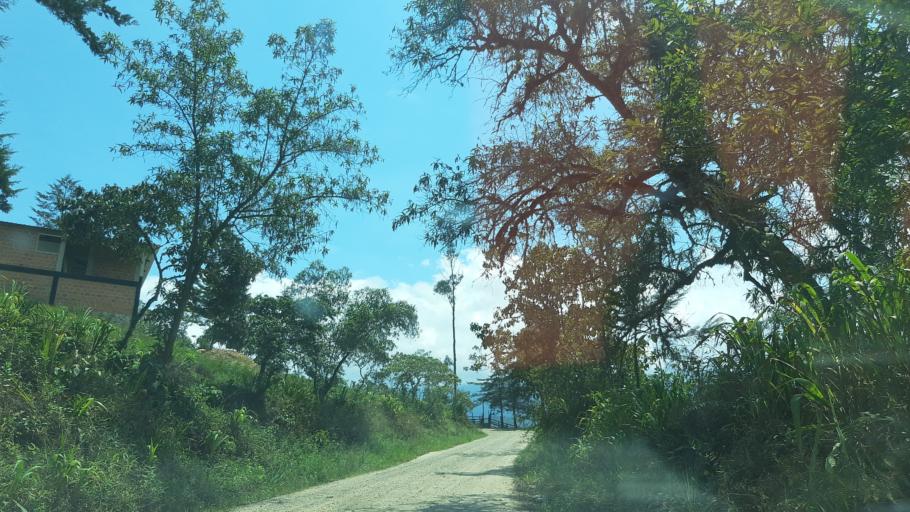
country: CO
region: Boyaca
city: Chinavita
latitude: 5.1290
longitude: -73.3733
